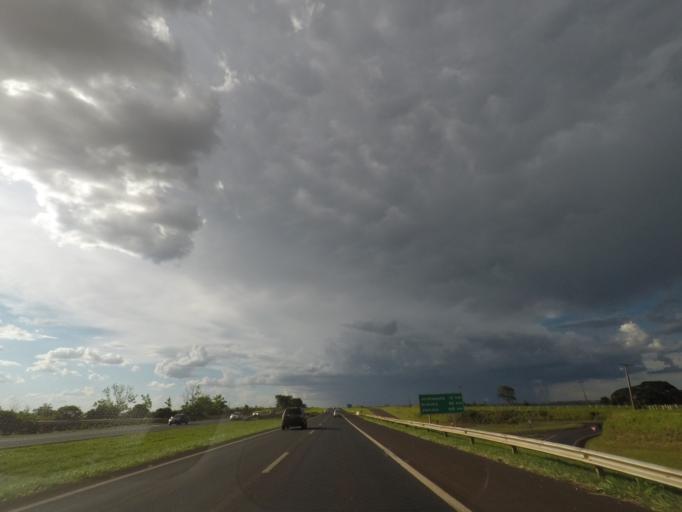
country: BR
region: Sao Paulo
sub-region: Jardinopolis
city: Jardinopolis
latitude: -21.0841
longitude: -47.8007
